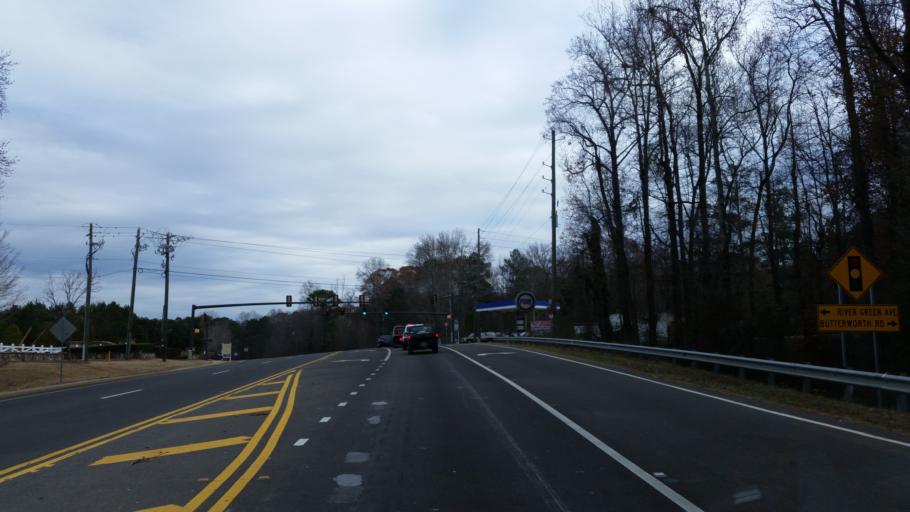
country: US
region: Georgia
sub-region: Cherokee County
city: Canton
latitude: 34.2125
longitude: -84.5287
